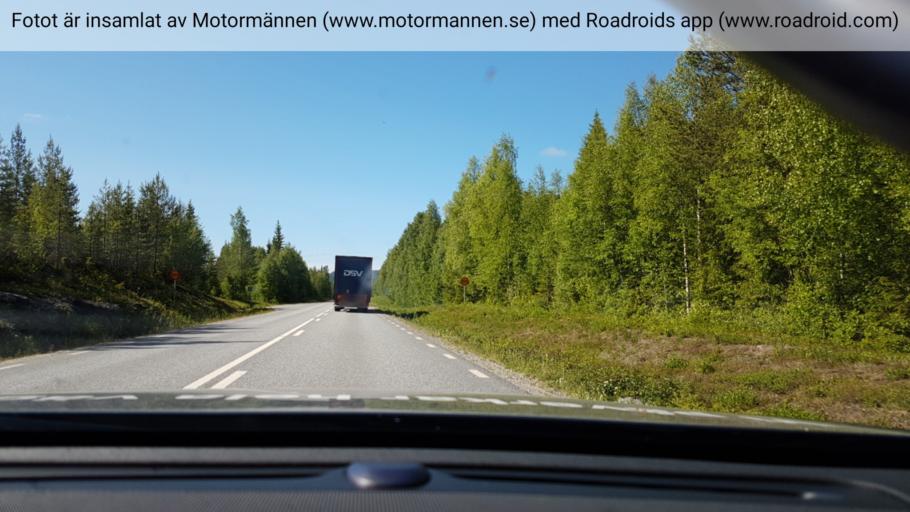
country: SE
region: Vaesterbotten
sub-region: Asele Kommun
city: Asele
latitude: 64.1904
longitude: 17.4716
